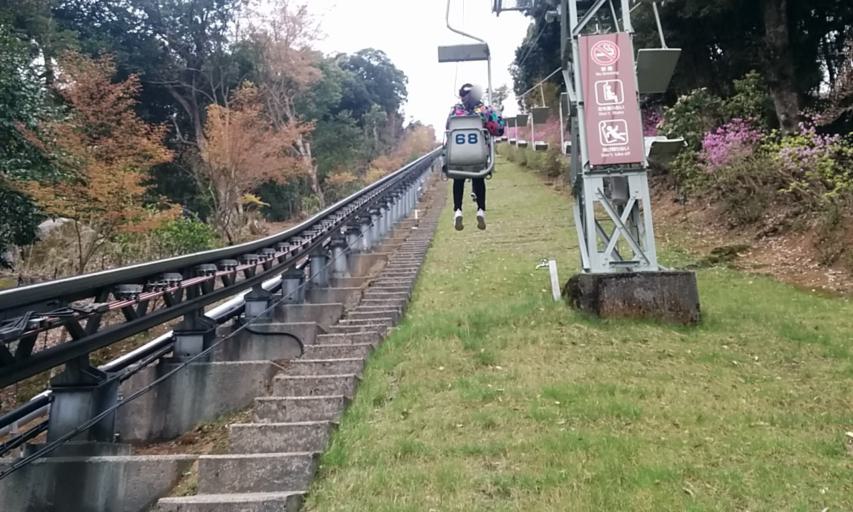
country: JP
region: Kyoto
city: Miyazu
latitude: 35.5544
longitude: 135.1829
